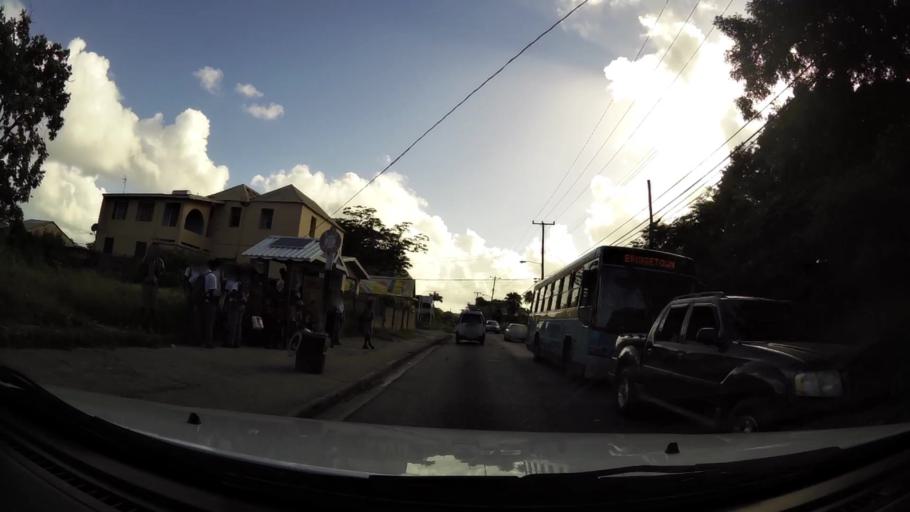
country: BB
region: Saint Michael
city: Bridgetown
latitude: 13.1026
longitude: -59.5939
